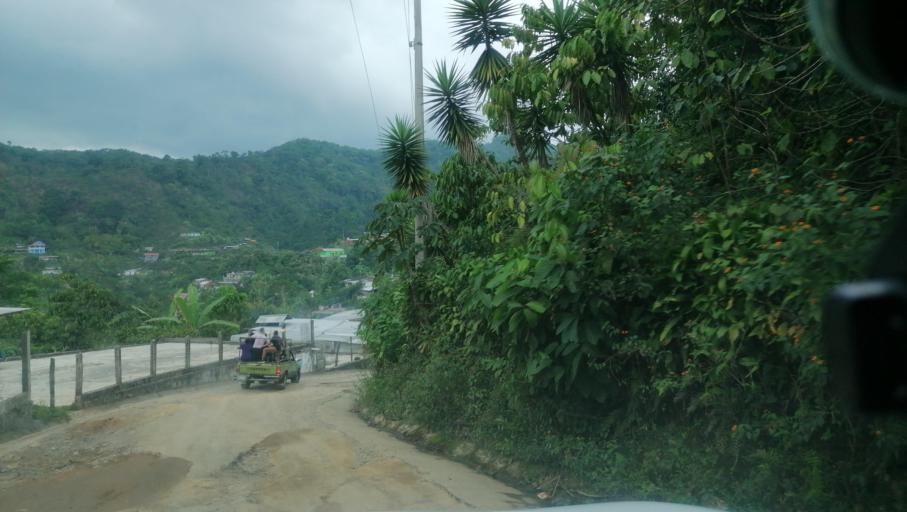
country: MX
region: Chiapas
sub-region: Cacahoatan
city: Benito Juarez
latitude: 15.0713
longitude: -92.1684
